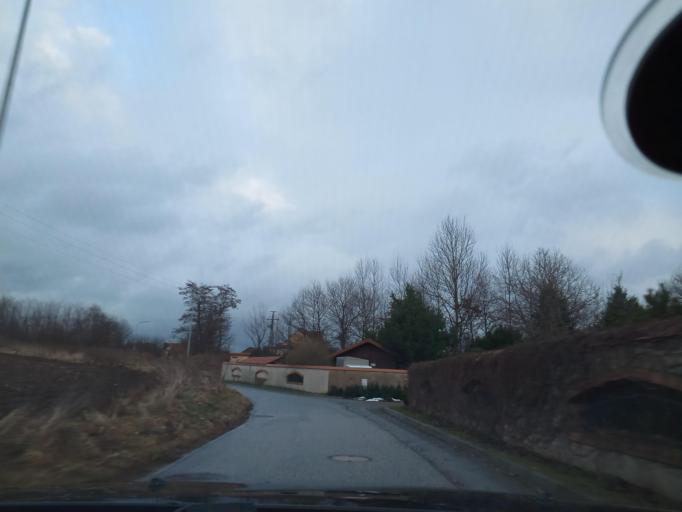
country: PL
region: Lesser Poland Voivodeship
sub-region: Powiat wielicki
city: Kokotow
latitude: 49.9994
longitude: 20.0857
